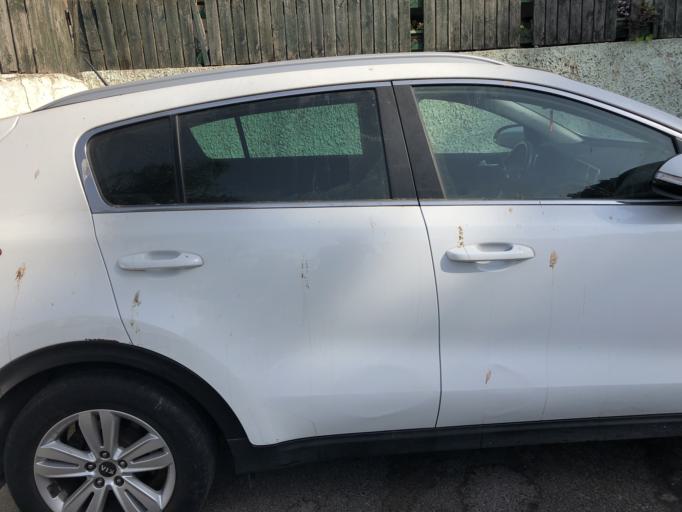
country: IL
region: Tel Aviv
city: Giv`atayim
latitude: 32.0689
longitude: 34.8206
